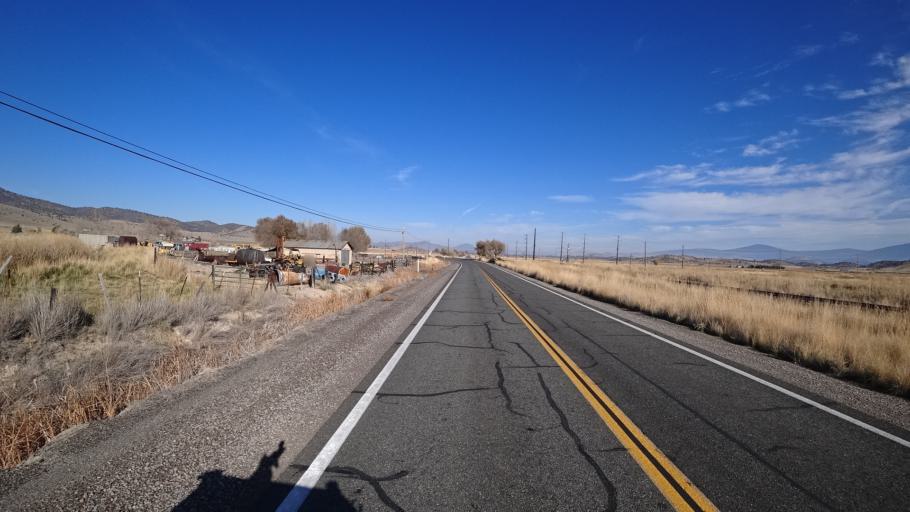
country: US
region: California
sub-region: Siskiyou County
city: Montague
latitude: 41.6017
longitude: -122.5235
